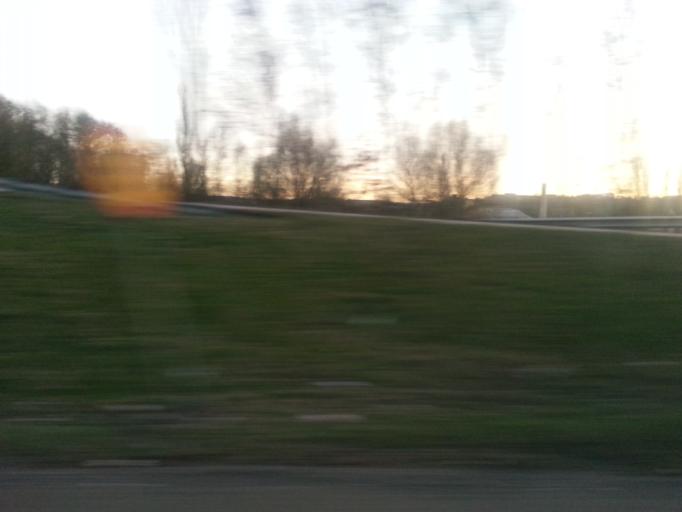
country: SE
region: Vaestra Goetaland
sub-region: Molndal
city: Moelndal
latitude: 57.6888
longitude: 12.0019
